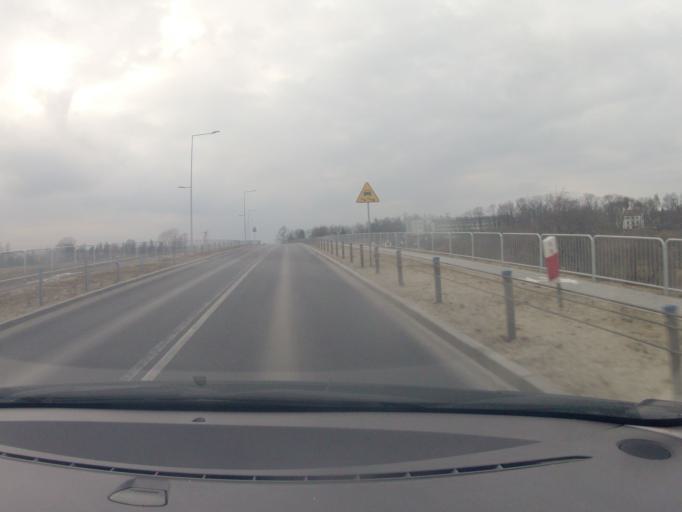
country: PL
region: Subcarpathian Voivodeship
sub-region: Powiat jasielski
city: Jaslo
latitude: 49.7487
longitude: 21.4836
